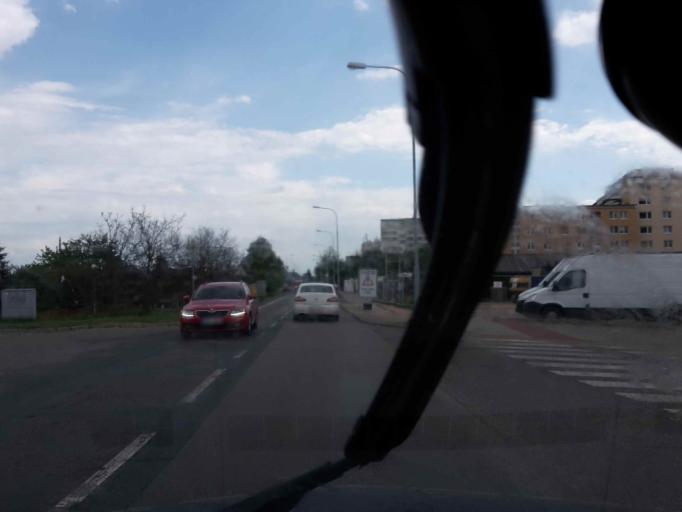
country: CZ
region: South Moravian
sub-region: Mesto Brno
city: Mokra Hora
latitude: 49.2363
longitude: 16.6277
